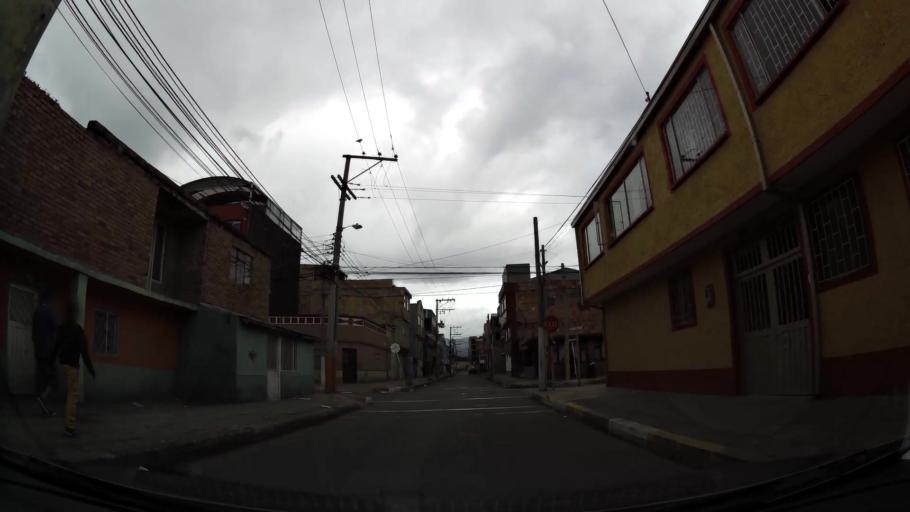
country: CO
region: Bogota D.C.
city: Barrio San Luis
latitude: 4.7063
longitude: -74.1041
